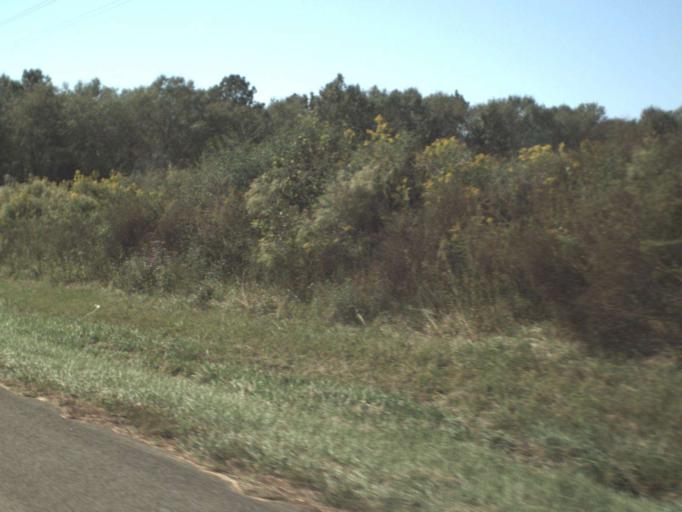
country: US
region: Alabama
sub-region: Geneva County
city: Samson
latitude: 30.9339
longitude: -86.1374
